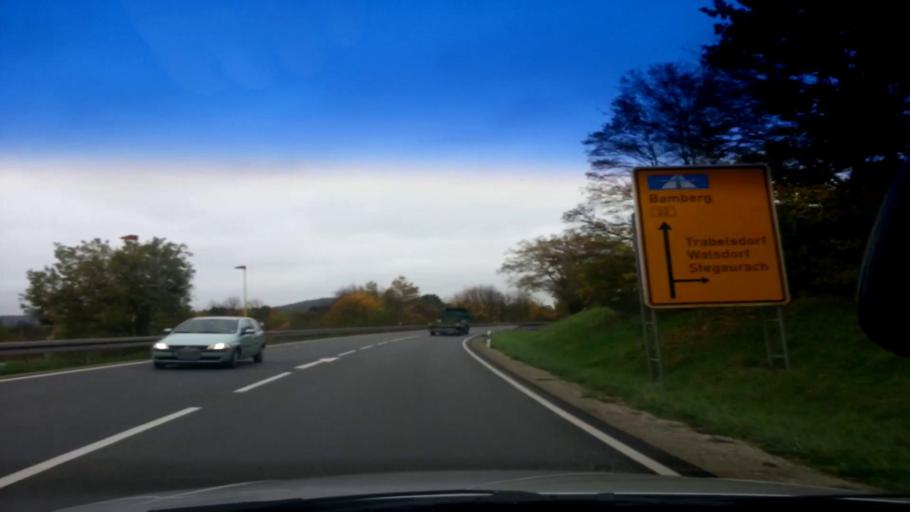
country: DE
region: Bavaria
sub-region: Upper Franconia
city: Stegaurach
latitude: 49.8646
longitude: 10.8595
